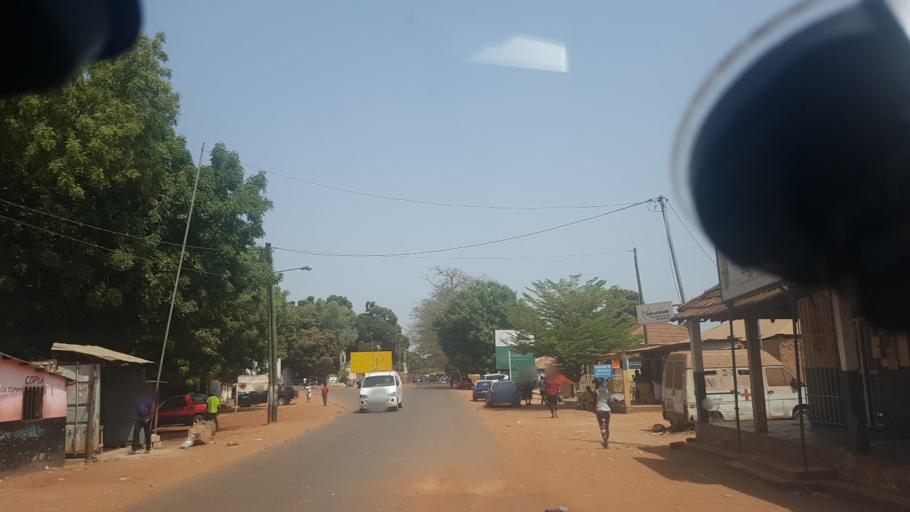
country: GW
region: Bissau
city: Bissau
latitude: 11.9546
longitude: -15.6489
